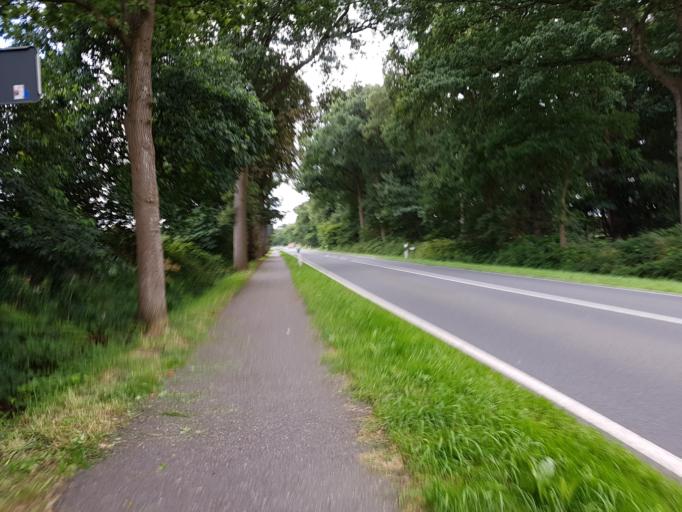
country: DE
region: Lower Saxony
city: Wittmund
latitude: 53.5159
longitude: 7.7934
